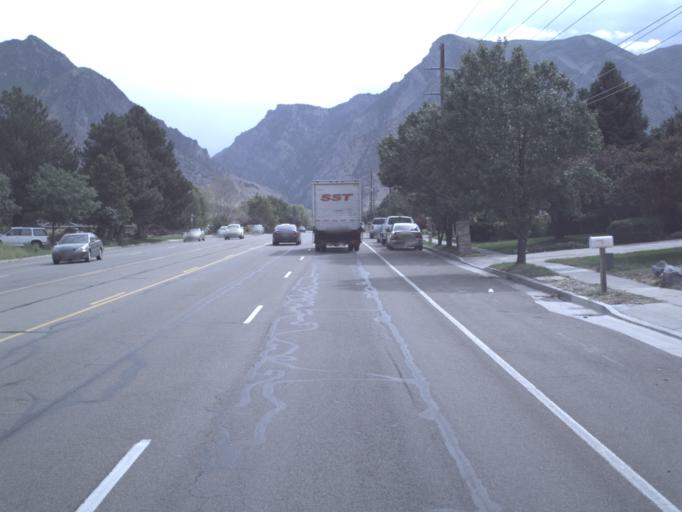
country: US
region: Utah
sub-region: Utah County
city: Highland
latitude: 40.4319
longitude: -111.7823
